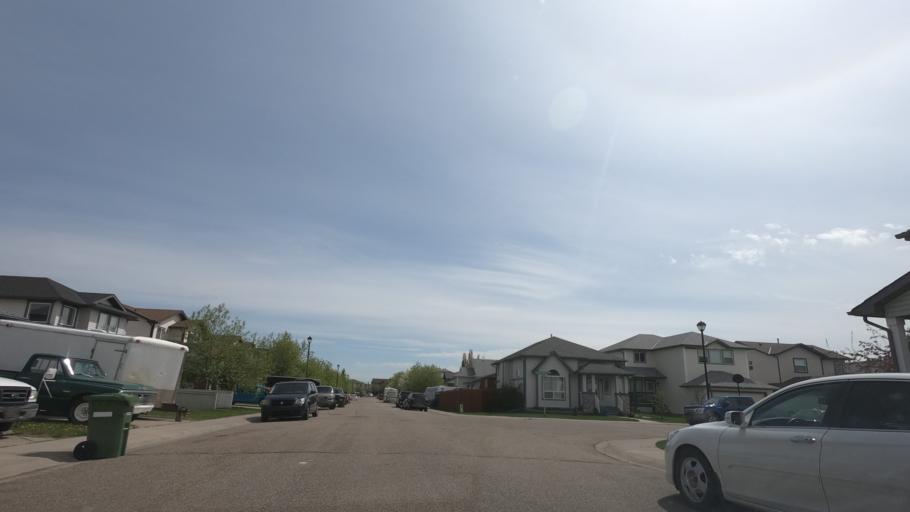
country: CA
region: Alberta
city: Airdrie
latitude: 51.3064
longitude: -114.0212
